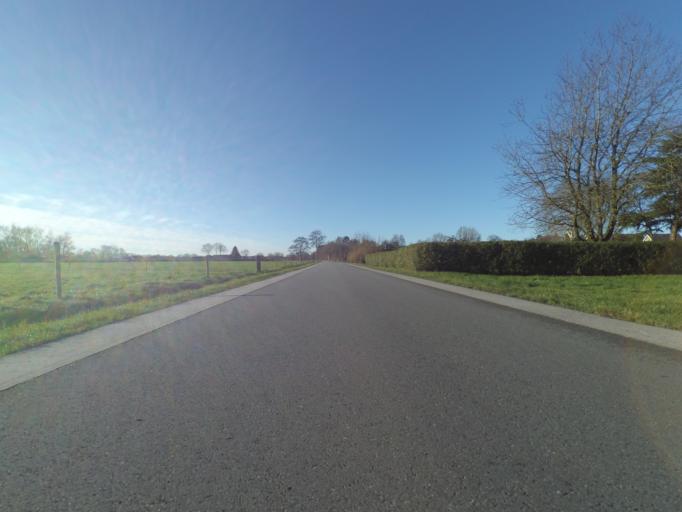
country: NL
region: Gelderland
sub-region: Gemeente Putten
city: Putten
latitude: 52.2439
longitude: 5.5631
